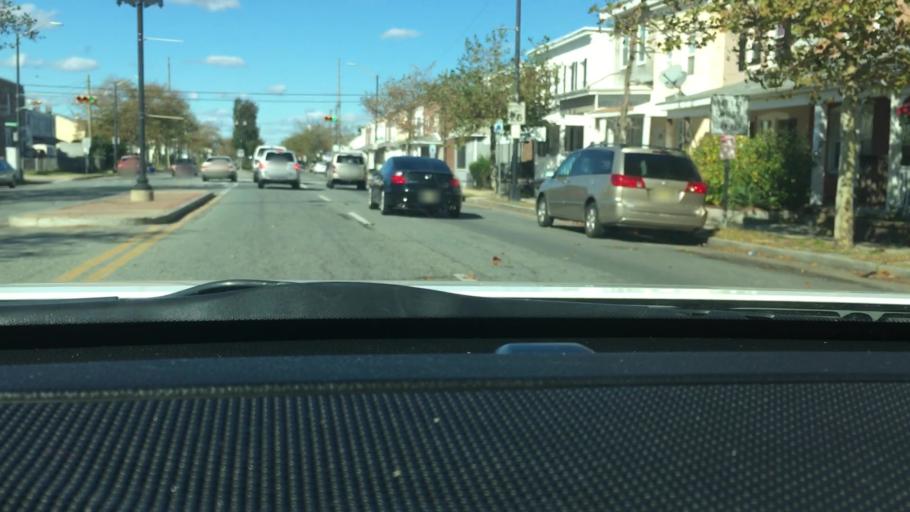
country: US
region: New Jersey
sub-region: Atlantic County
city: Atlantic City
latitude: 39.3662
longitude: -74.4356
